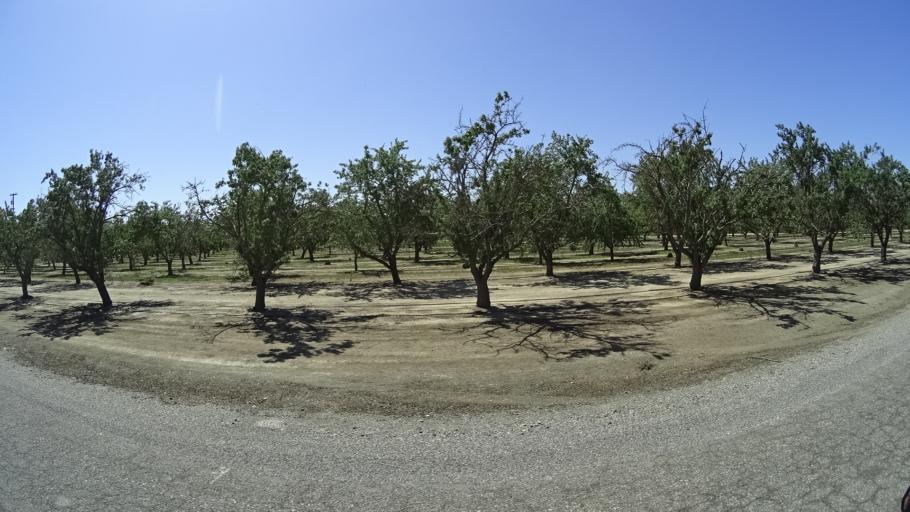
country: US
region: California
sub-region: Glenn County
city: Orland
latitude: 39.6816
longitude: -122.1238
